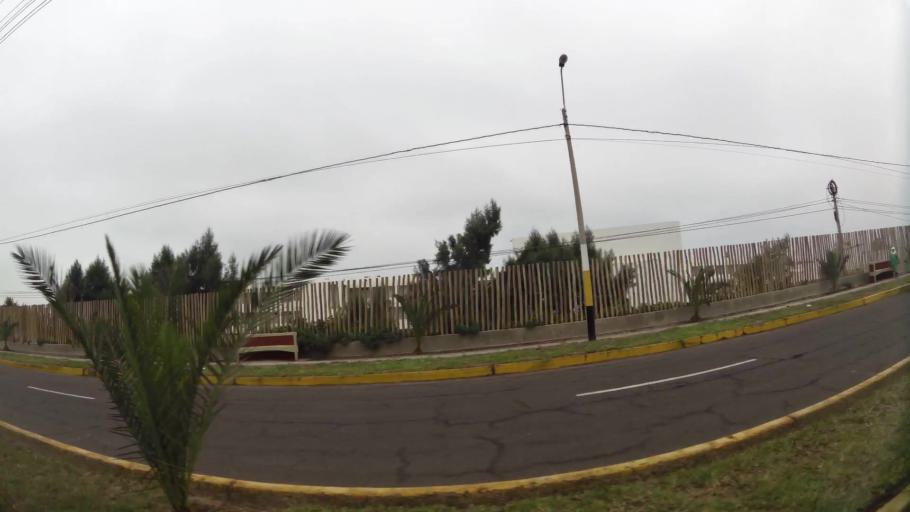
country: PE
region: Ica
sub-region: Provincia de Pisco
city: Paracas
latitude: -13.8299
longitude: -76.2460
